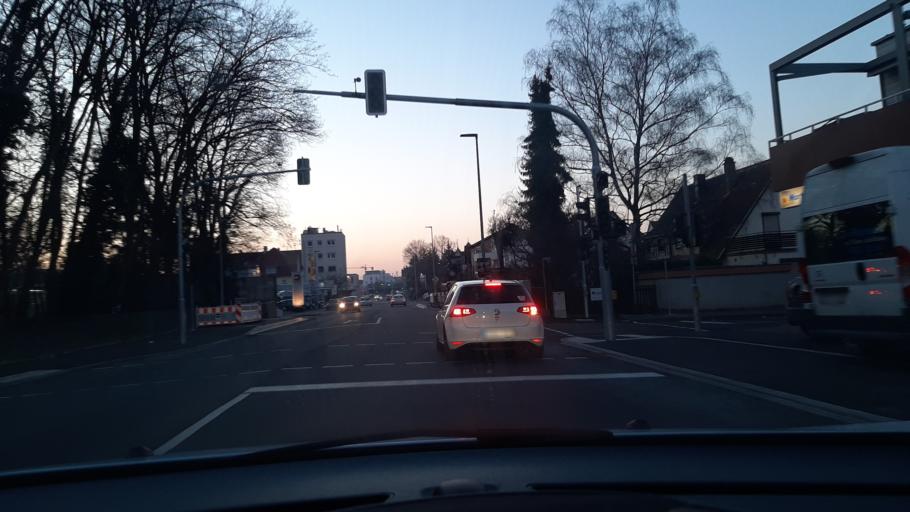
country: DE
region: Baden-Wuerttemberg
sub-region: Regierungsbezirk Stuttgart
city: Eislingen
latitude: 48.6923
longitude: 9.7142
